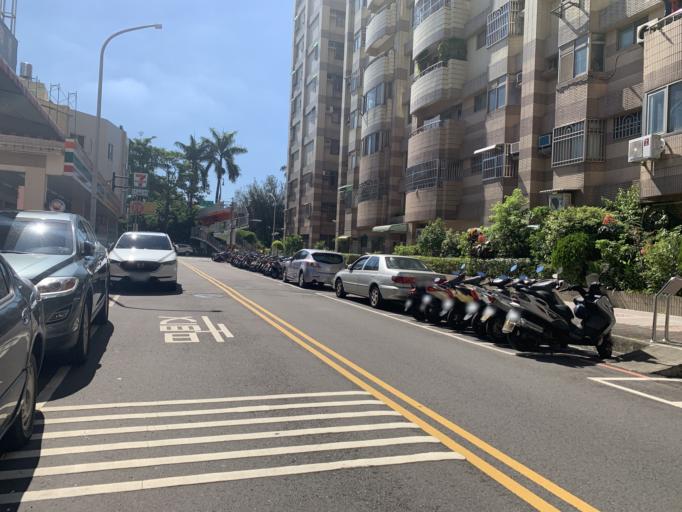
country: TW
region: Taiwan
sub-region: Taichung City
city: Taichung
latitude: 24.1454
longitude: 120.6917
